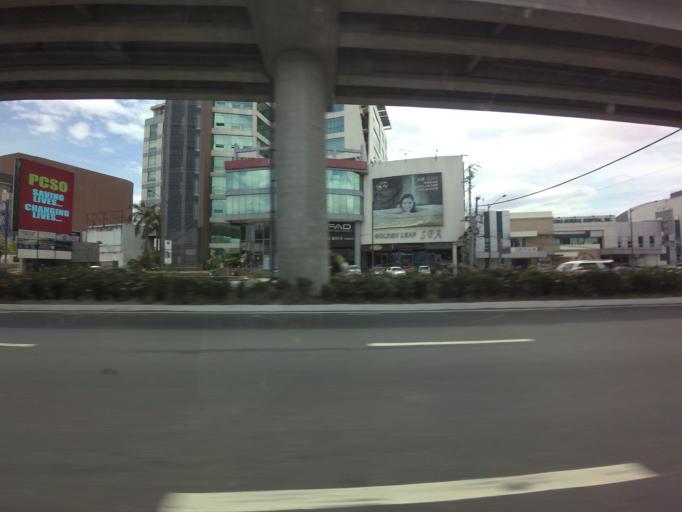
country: PH
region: Metro Manila
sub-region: Marikina
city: Calumpang
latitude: 14.6194
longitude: 121.0961
